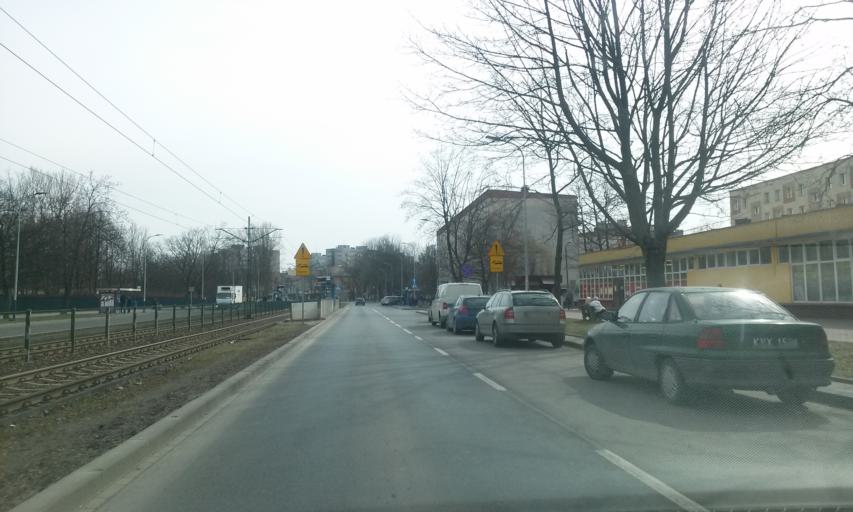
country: PL
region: Lesser Poland Voivodeship
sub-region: Powiat krakowski
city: Michalowice
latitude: 50.0930
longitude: 20.0148
